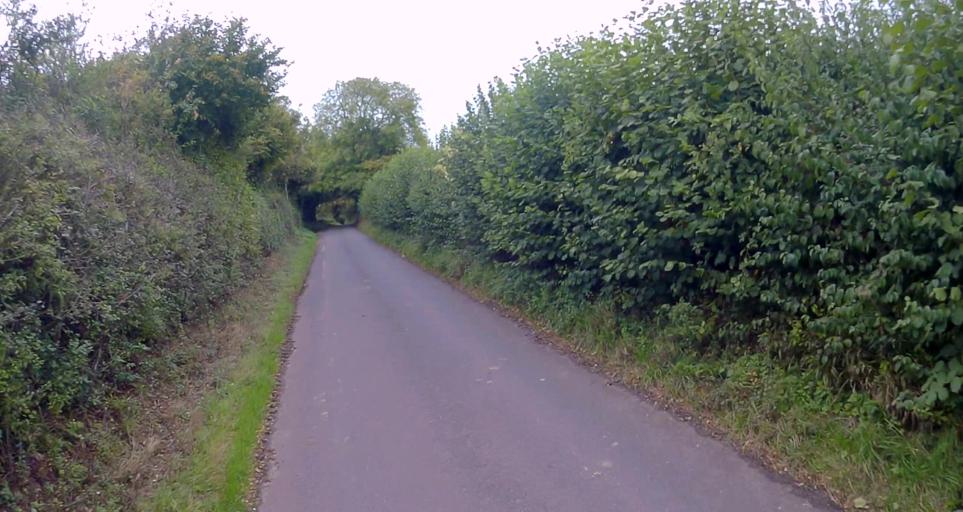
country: GB
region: England
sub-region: Hampshire
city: Four Marks
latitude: 51.1559
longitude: -1.0859
